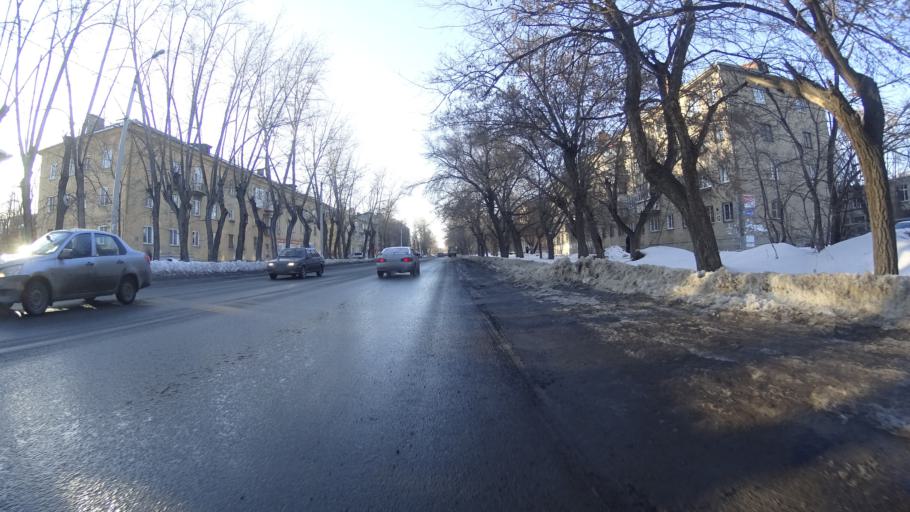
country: RU
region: Chelyabinsk
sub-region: Gorod Chelyabinsk
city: Chelyabinsk
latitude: 55.1277
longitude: 61.4701
